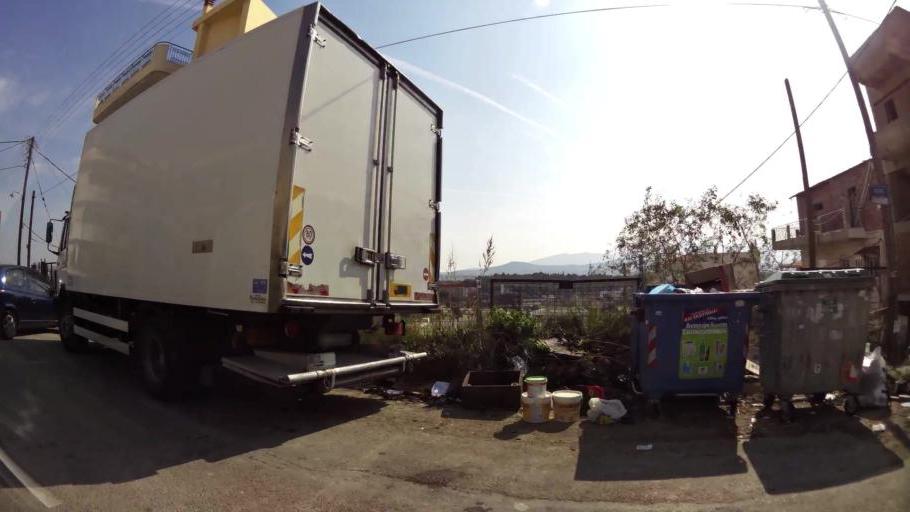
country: GR
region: Attica
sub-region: Nomarchia Athinas
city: Kamateron
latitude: 38.0505
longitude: 23.7112
